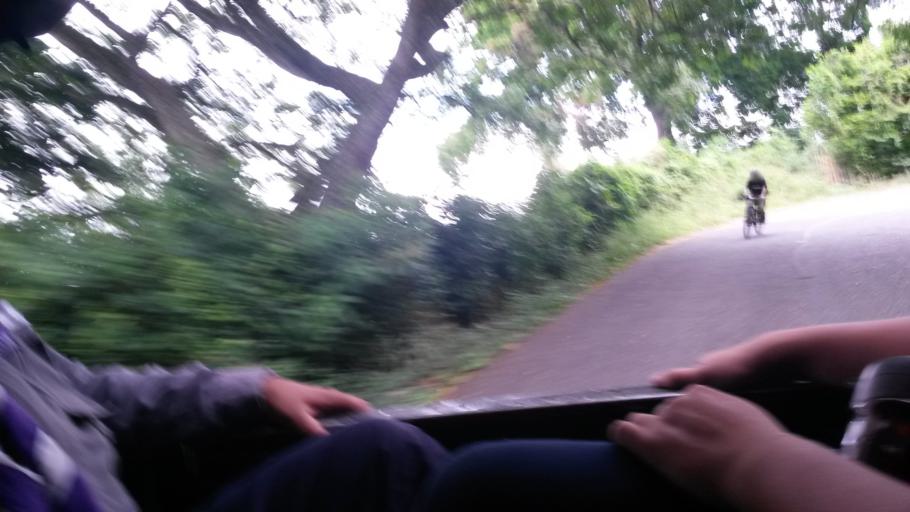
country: CO
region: Quindio
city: Buenavista
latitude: 4.3704
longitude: -75.7533
